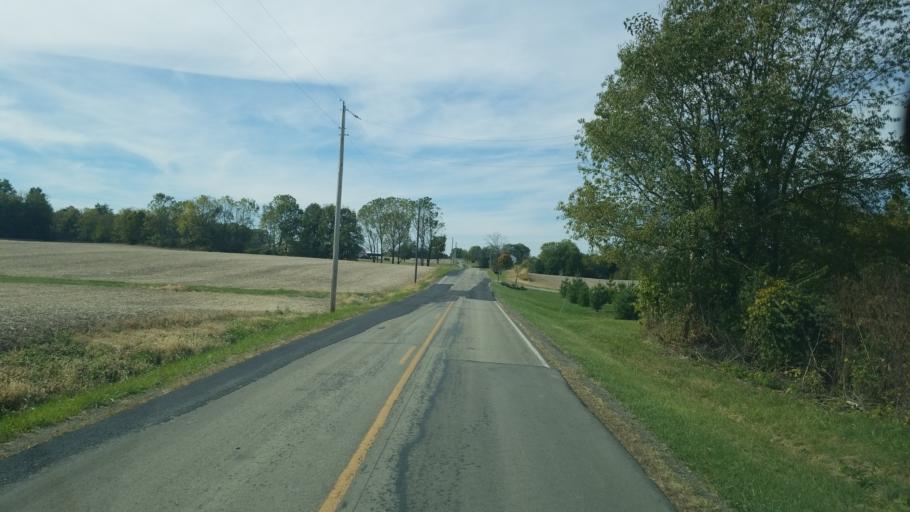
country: US
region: Ohio
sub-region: Highland County
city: Leesburg
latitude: 39.3294
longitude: -83.4905
